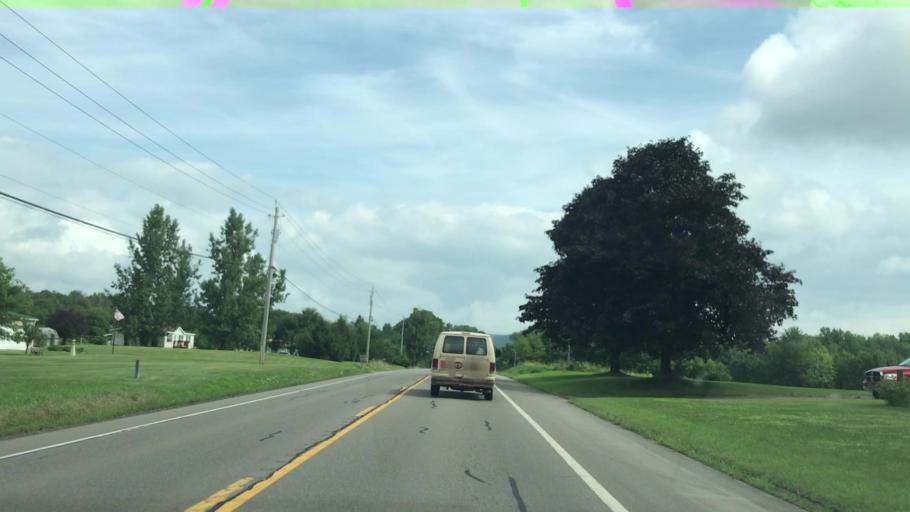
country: US
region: New York
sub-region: Steuben County
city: Bath
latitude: 42.4791
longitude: -77.2929
